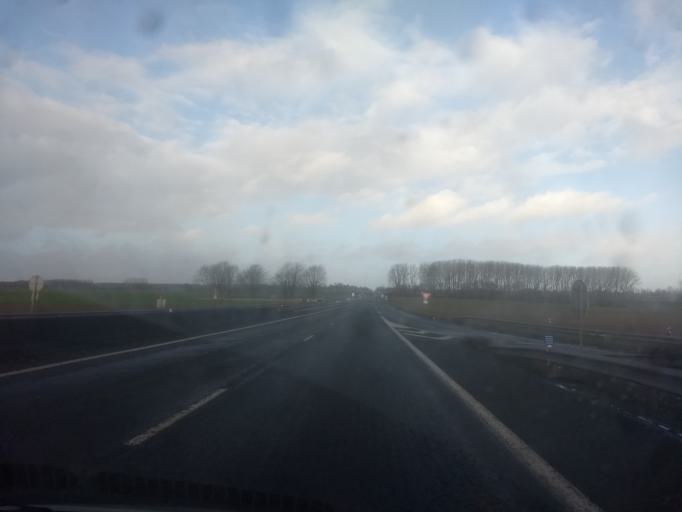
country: FR
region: Nord-Pas-de-Calais
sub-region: Departement du Pas-de-Calais
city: Thelus
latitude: 50.3444
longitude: 2.7841
